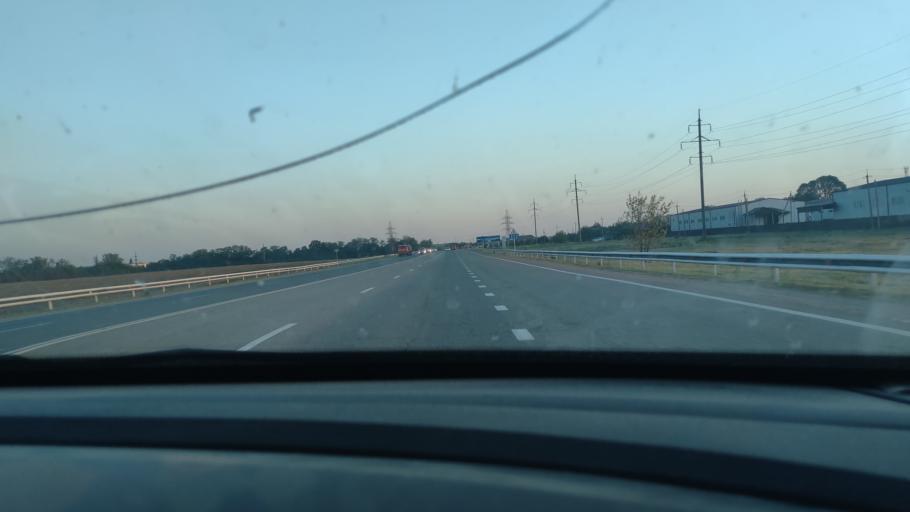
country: RU
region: Krasnodarskiy
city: Timashevsk
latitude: 45.6158
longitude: 38.9867
